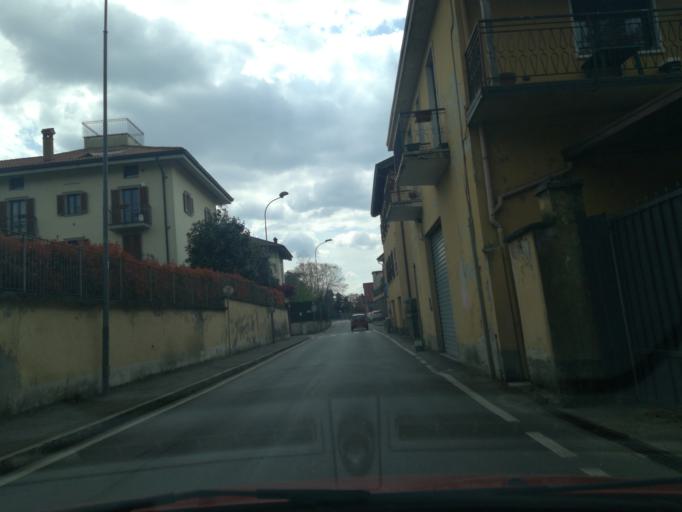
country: IT
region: Lombardy
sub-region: Provincia di Monza e Brianza
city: Lesmo
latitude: 45.6313
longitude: 9.3033
